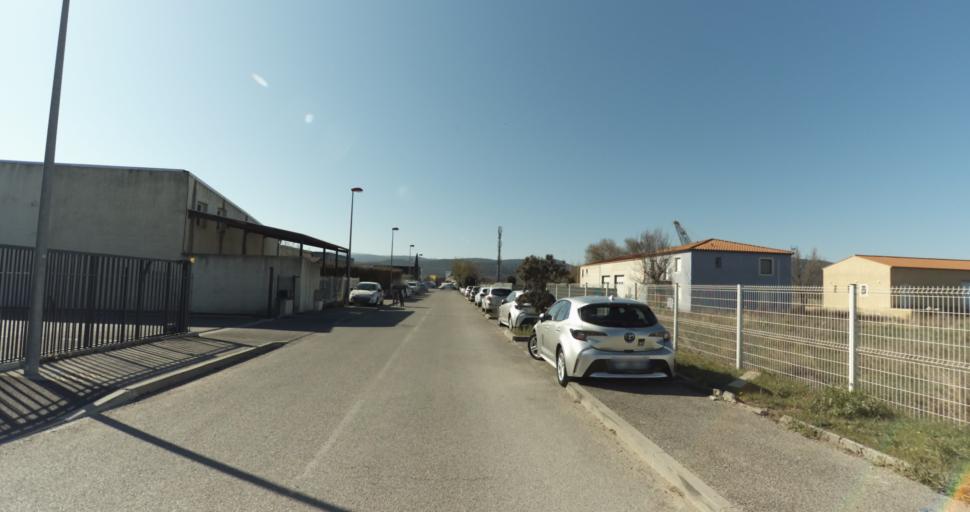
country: FR
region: Provence-Alpes-Cote d'Azur
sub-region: Departement des Bouches-du-Rhone
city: Peyrolles-en-Provence
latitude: 43.6572
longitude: 5.5767
